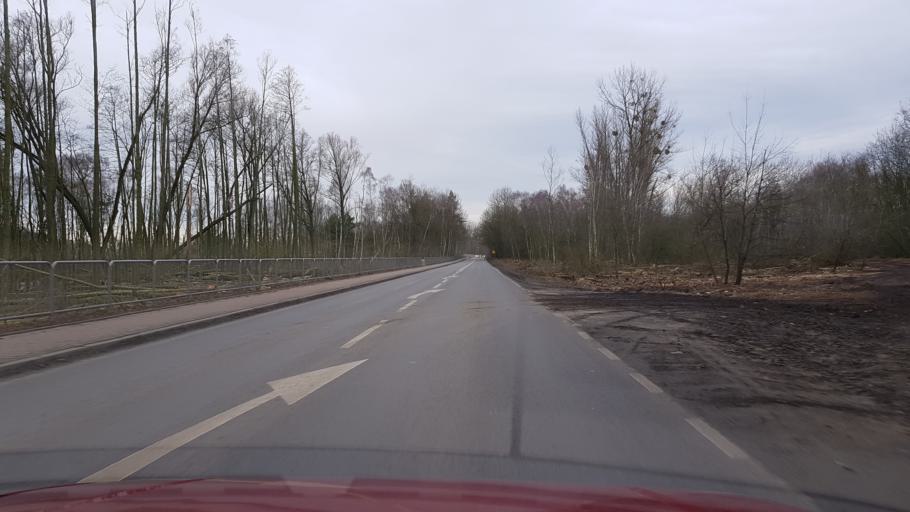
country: PL
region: West Pomeranian Voivodeship
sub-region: Powiat policki
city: Police
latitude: 53.5642
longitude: 14.5604
